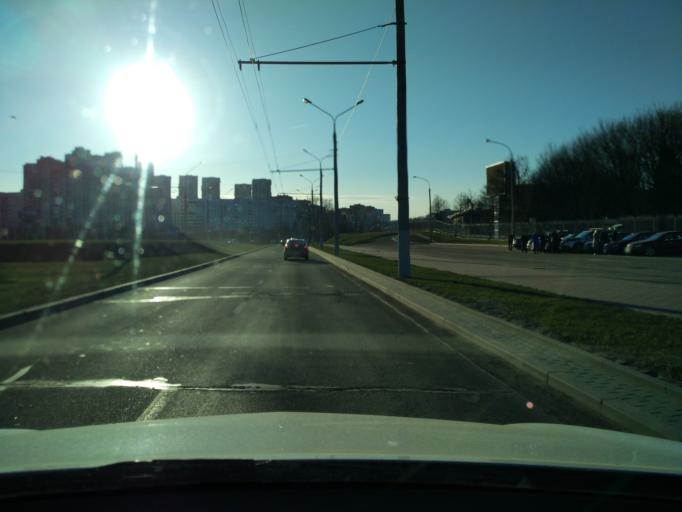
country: BY
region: Minsk
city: Minsk
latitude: 53.9298
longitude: 27.5168
